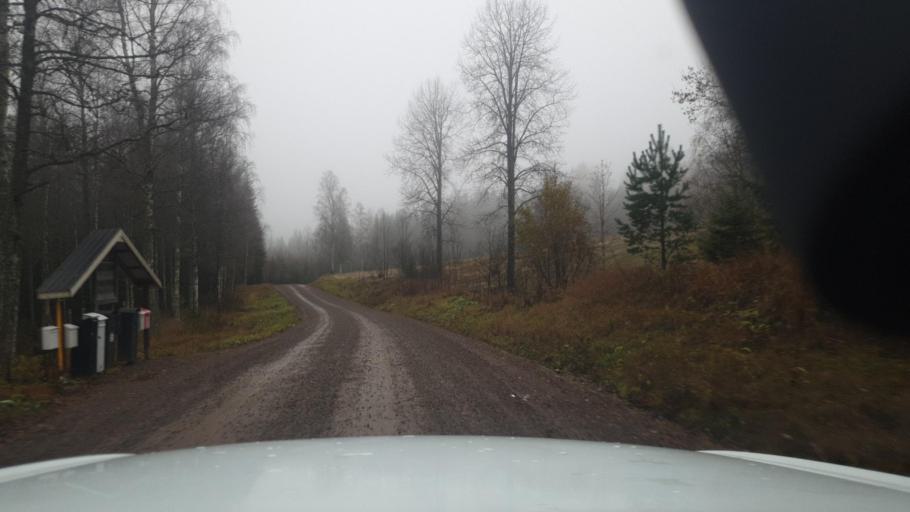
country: SE
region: Vaermland
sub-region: Arvika Kommun
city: Arvika
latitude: 59.9994
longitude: 12.6590
